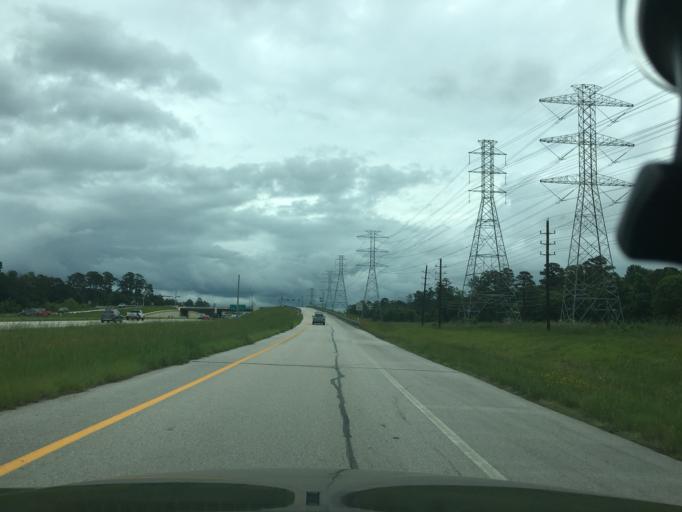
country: US
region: Texas
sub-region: Harris County
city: Spring
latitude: 30.0894
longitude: -95.4610
